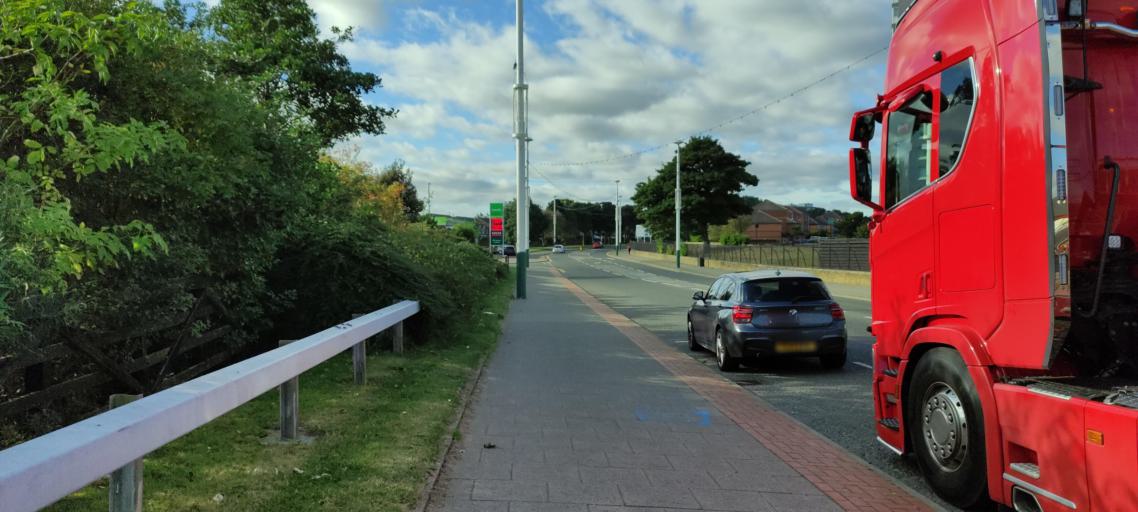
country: GB
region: England
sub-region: Sunderland
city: Sunderland
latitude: 54.9176
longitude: -1.3699
